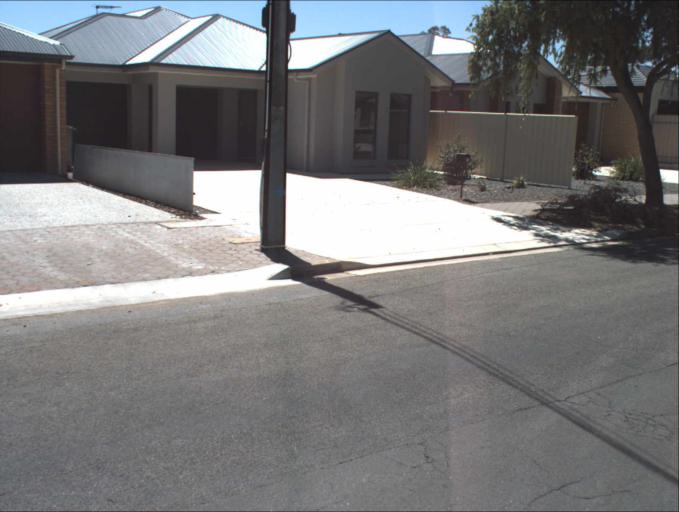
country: AU
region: South Australia
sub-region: Port Adelaide Enfield
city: Klemzig
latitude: -34.8686
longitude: 138.6220
